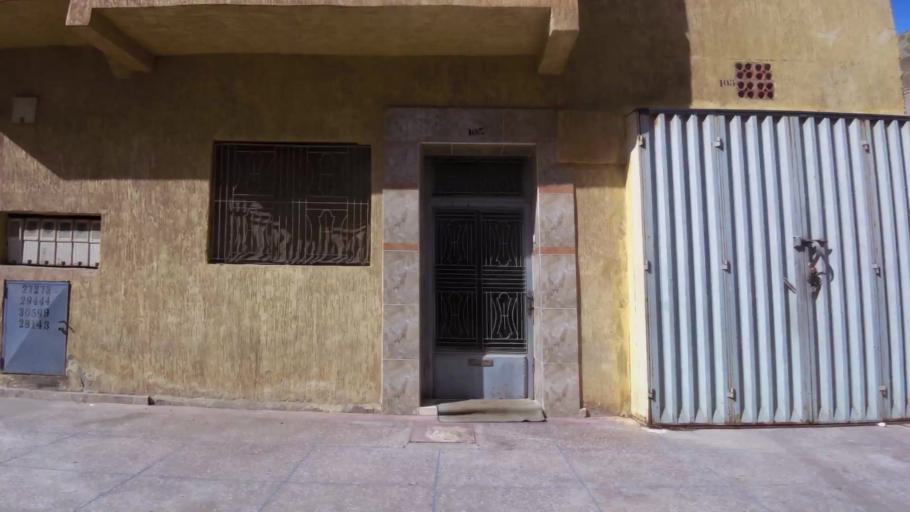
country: MA
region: Chaouia-Ouardigha
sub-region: Settat Province
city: Berrechid
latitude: 33.2622
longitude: -7.5673
